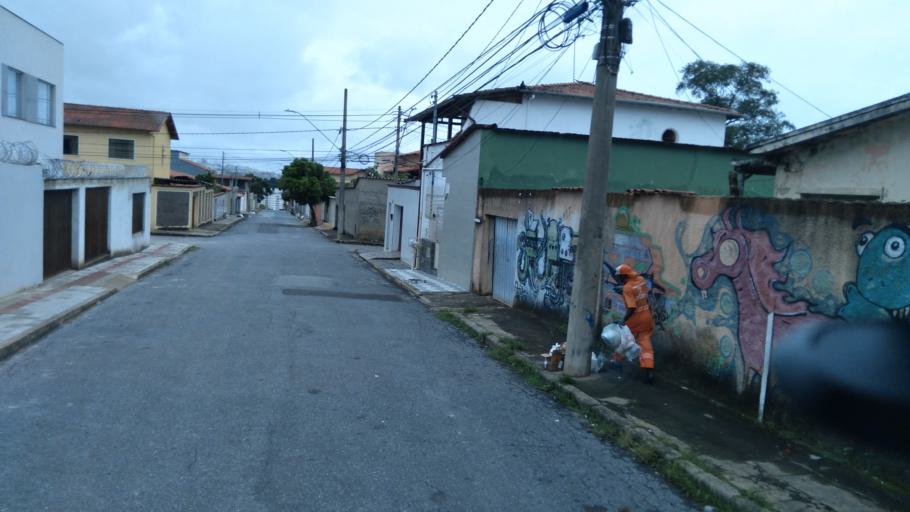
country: BR
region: Minas Gerais
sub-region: Belo Horizonte
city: Belo Horizonte
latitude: -19.9140
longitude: -43.8972
